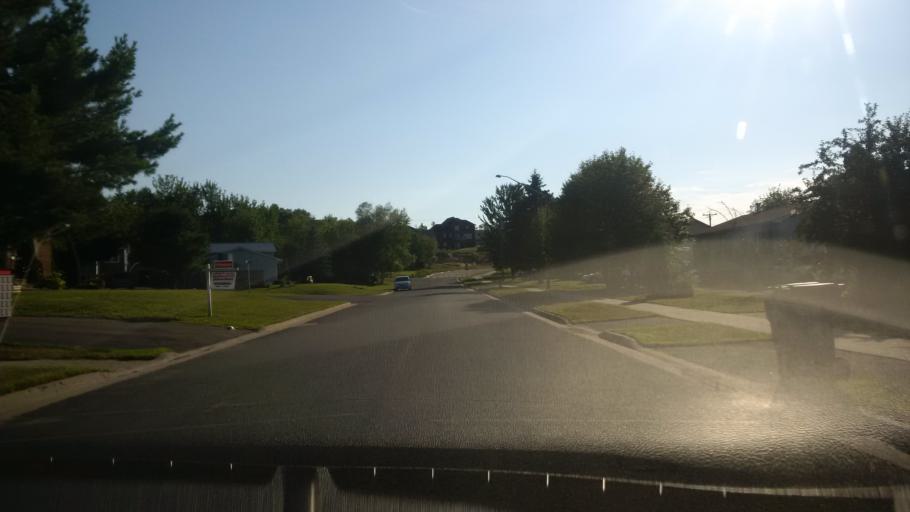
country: CA
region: New Brunswick
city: Fredericton
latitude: 45.9014
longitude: -66.6900
